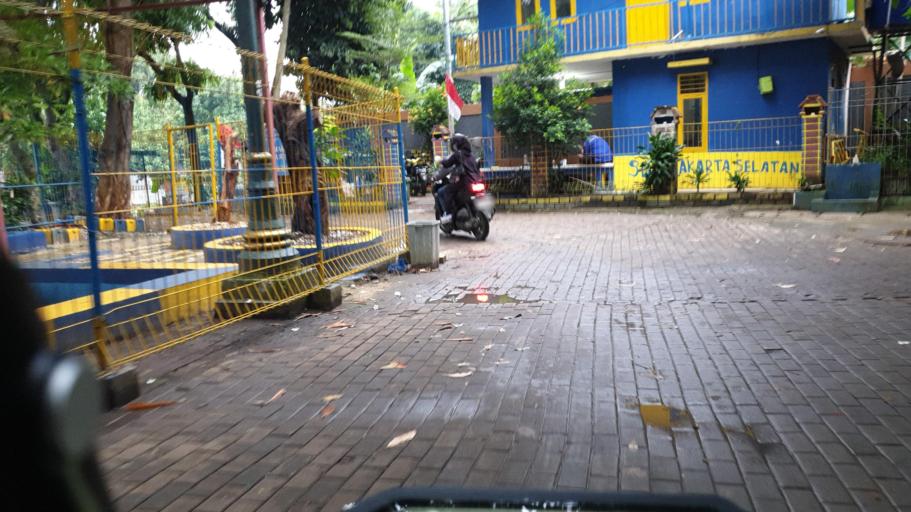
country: ID
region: West Java
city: Depok
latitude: -6.3387
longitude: 106.8267
